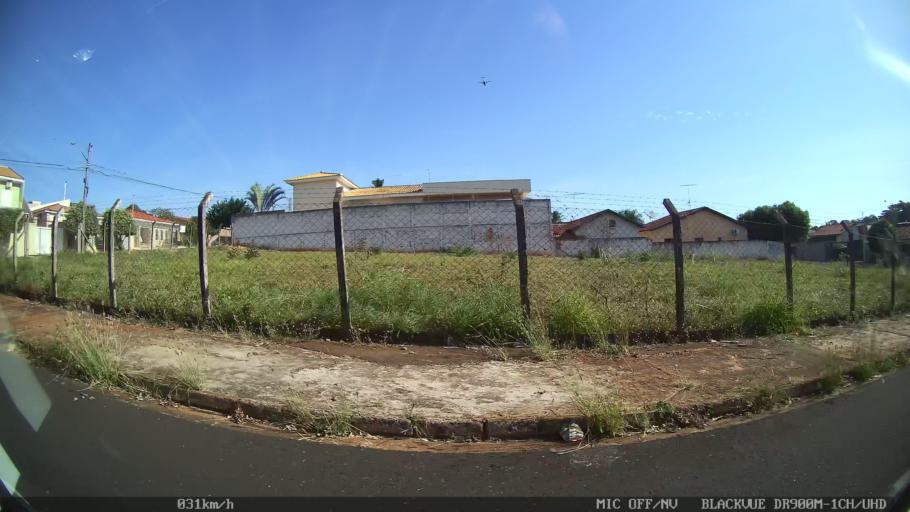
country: BR
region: Sao Paulo
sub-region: Sao Jose Do Rio Preto
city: Sao Jose do Rio Preto
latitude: -20.7794
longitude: -49.3575
